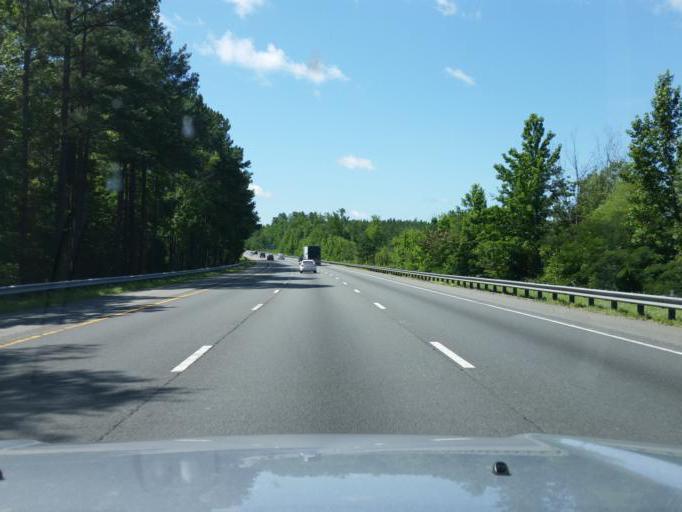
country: US
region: Virginia
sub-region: Spotsylvania County
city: Spotsylvania Courthouse
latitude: 38.1641
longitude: -77.5070
